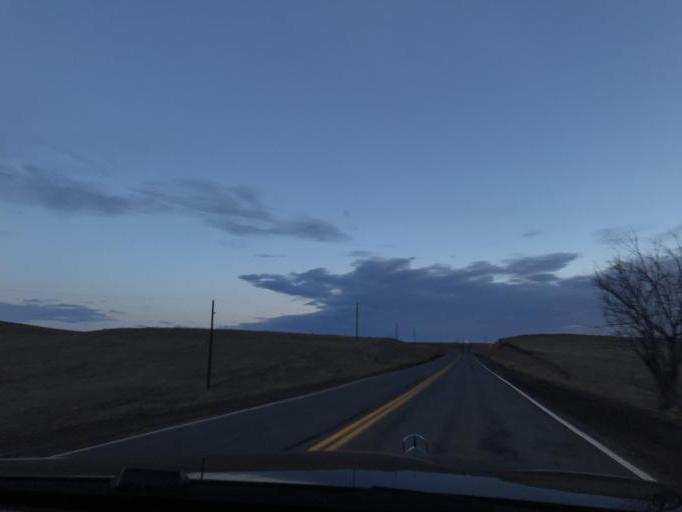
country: US
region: Colorado
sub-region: Boulder County
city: Superior
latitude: 39.8946
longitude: -105.1656
